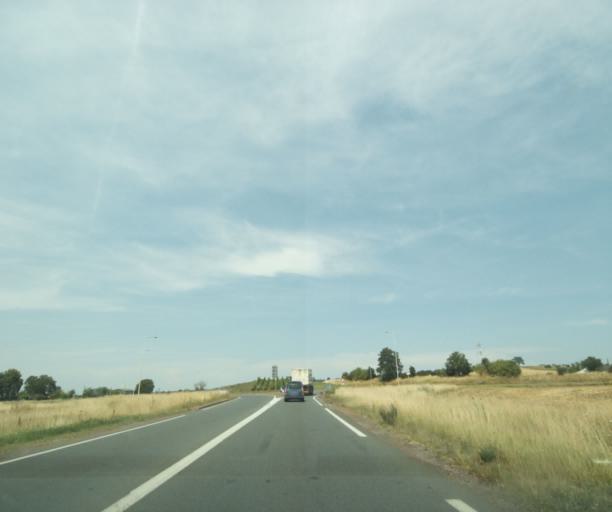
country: FR
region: Poitou-Charentes
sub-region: Departement de la Vienne
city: Chatellerault
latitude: 46.7980
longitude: 0.5609
